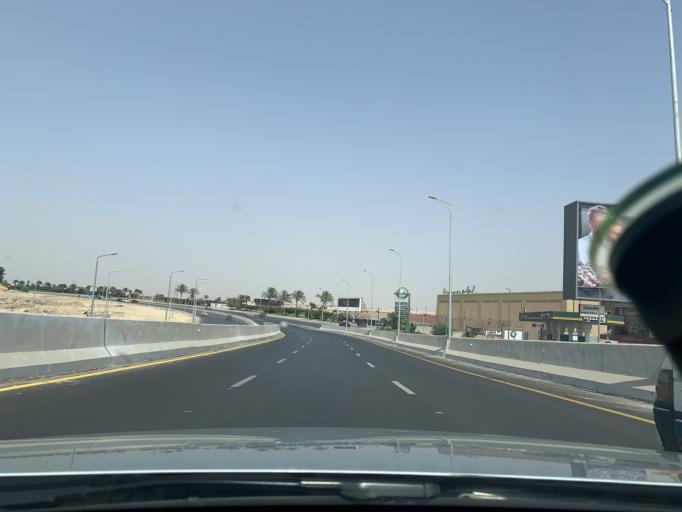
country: EG
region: Muhafazat al Qalyubiyah
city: Al Khankah
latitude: 30.0912
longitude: 31.3798
